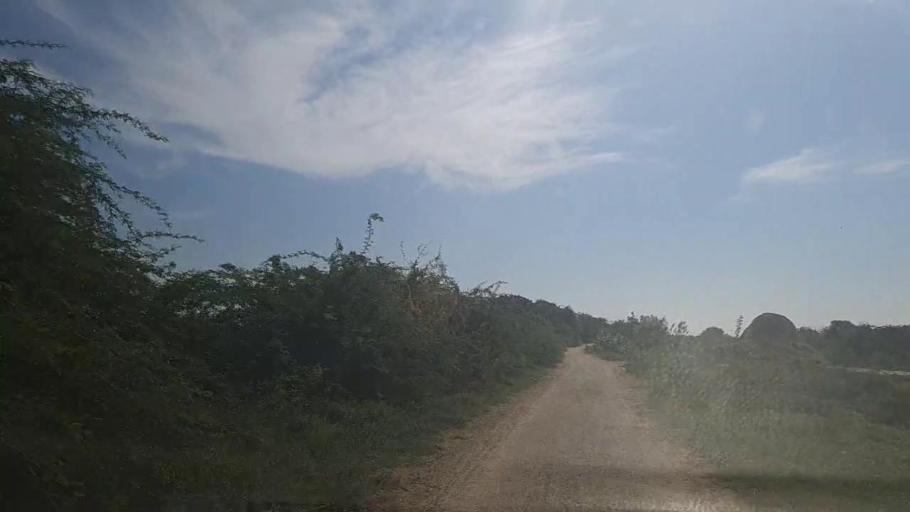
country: PK
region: Sindh
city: Mirpur Batoro
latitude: 24.6664
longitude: 68.1848
